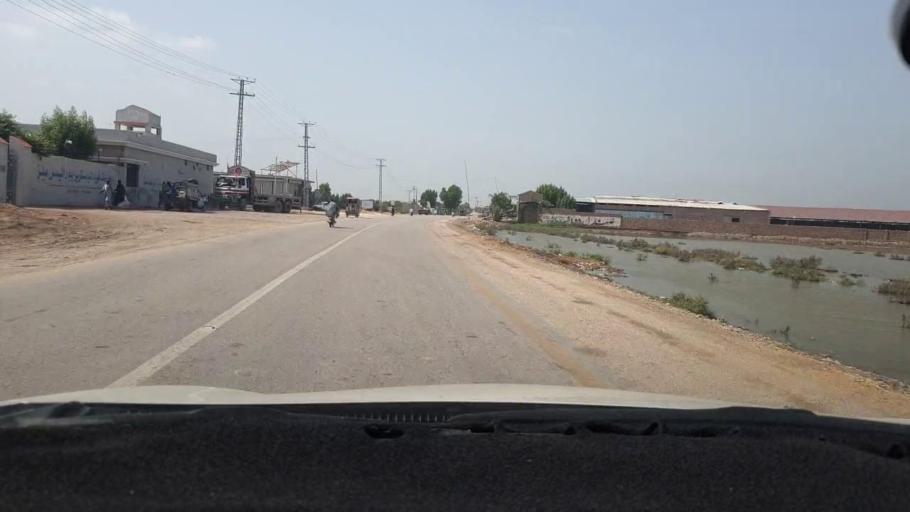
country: PK
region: Sindh
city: Mirpur Khas
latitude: 25.5499
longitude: 69.0473
